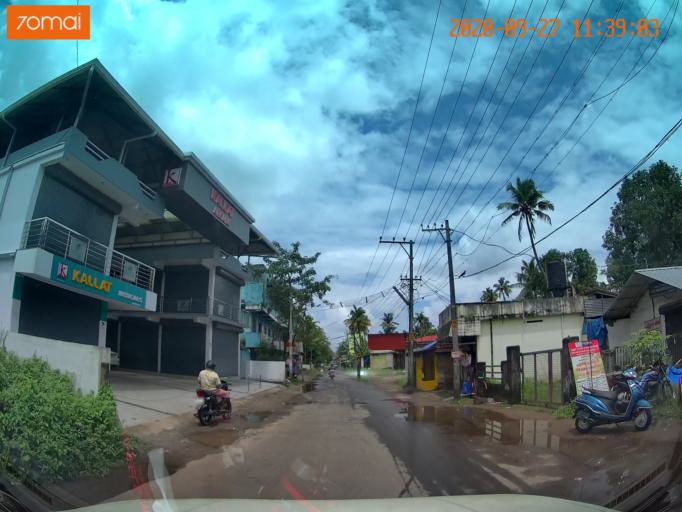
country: IN
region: Kerala
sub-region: Thrissur District
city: Thanniyam
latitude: 10.4631
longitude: 76.1191
